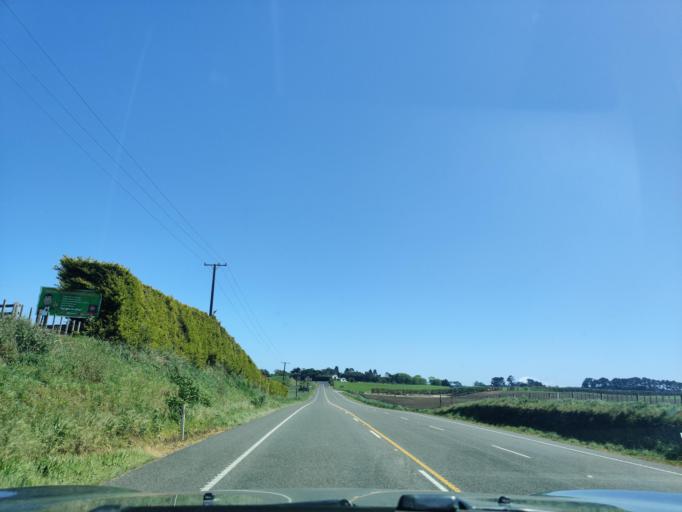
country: NZ
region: Taranaki
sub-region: South Taranaki District
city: Patea
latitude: -39.7655
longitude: 174.6483
